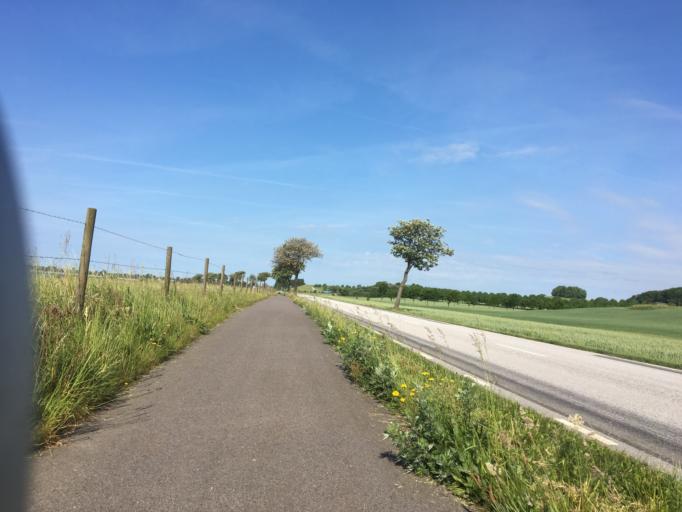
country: SE
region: Skane
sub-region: Skurups Kommun
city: Rydsgard
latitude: 55.4181
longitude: 13.6698
